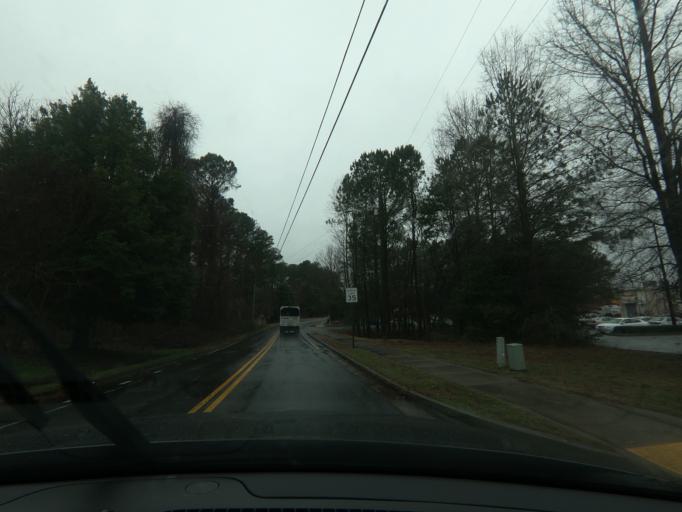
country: US
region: Georgia
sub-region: Cobb County
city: Acworth
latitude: 34.0333
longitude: -84.6769
